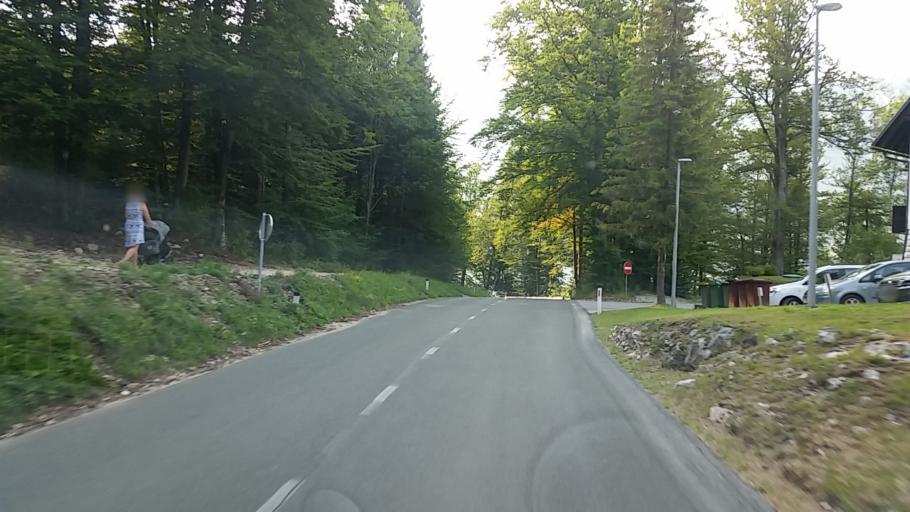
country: SI
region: Bohinj
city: Bohinjska Bistrica
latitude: 46.2770
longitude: 13.8813
